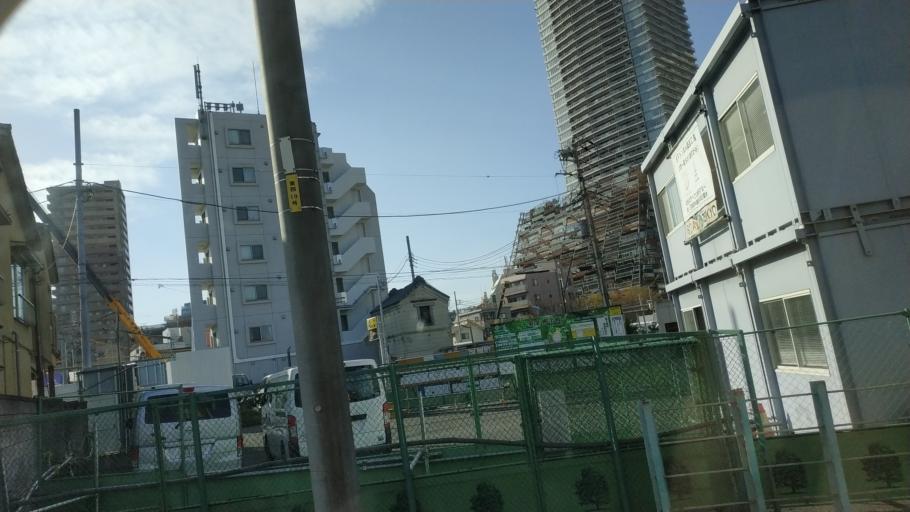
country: JP
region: Tokyo
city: Tokyo
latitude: 35.7244
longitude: 139.7180
